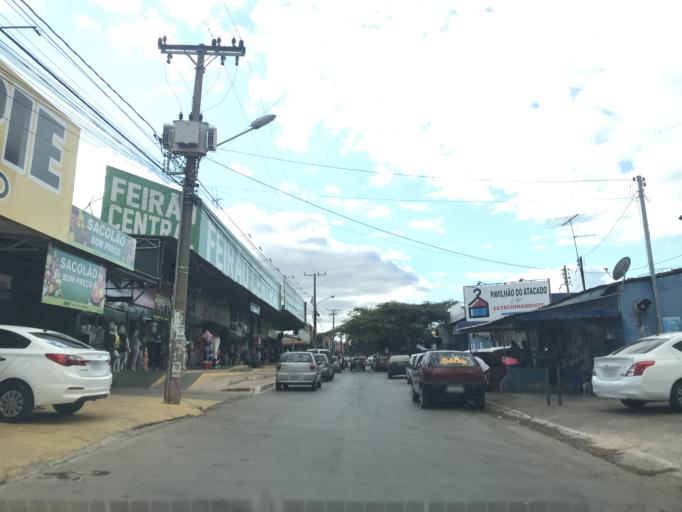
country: BR
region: Federal District
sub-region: Brasilia
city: Brasilia
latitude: -15.8089
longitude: -48.0782
